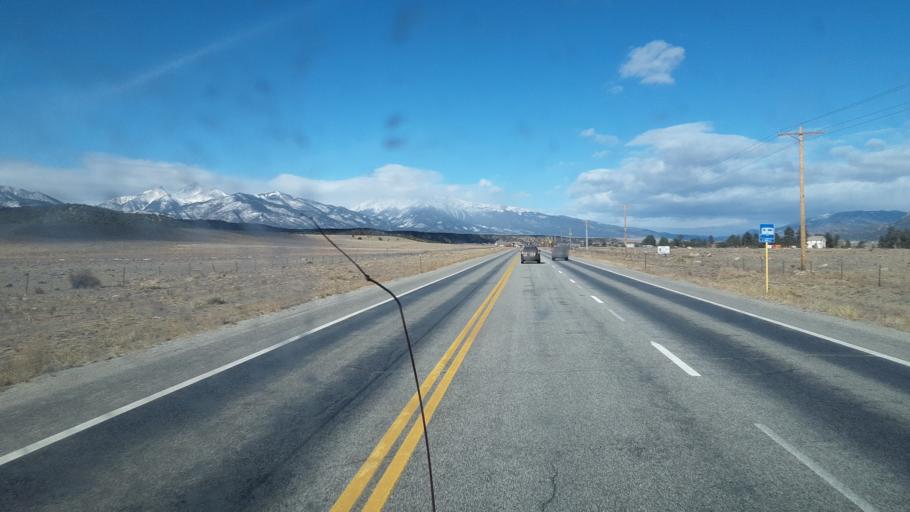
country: US
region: Colorado
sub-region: Chaffee County
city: Buena Vista
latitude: 38.7557
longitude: -106.0837
